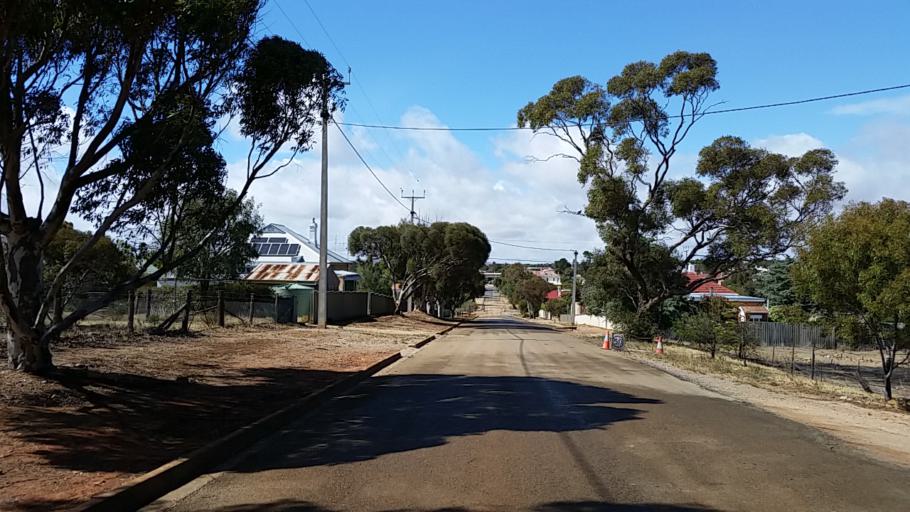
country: AU
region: South Australia
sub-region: Peterborough
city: Peterborough
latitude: -32.9692
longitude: 138.8359
